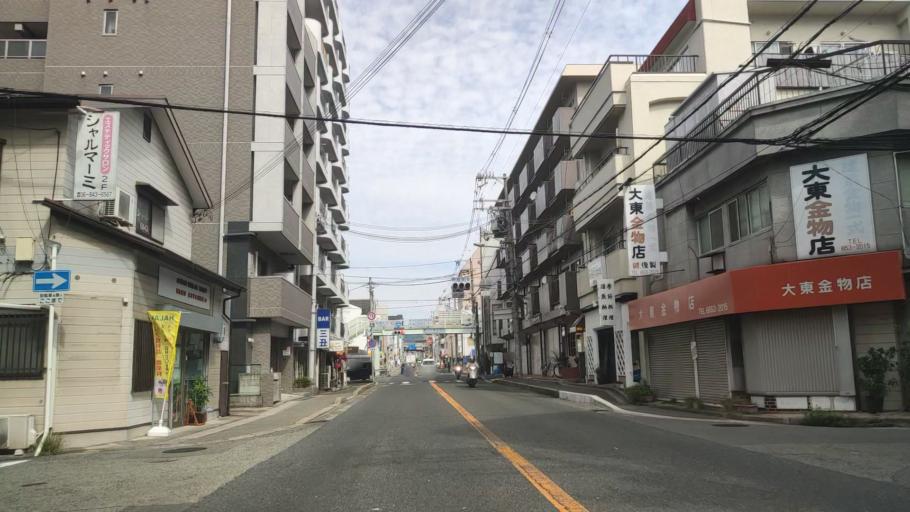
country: JP
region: Osaka
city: Toyonaka
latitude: 34.7968
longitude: 135.4491
